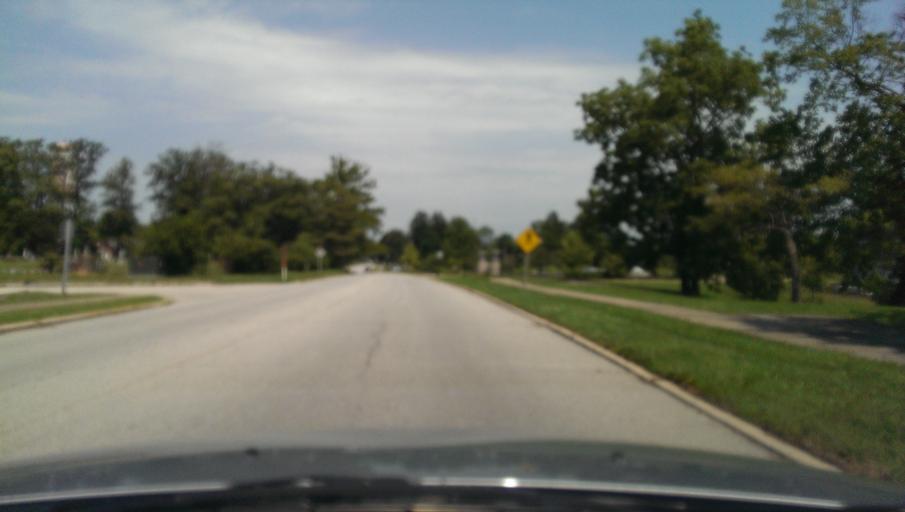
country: US
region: Indiana
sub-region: Marion County
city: Lawrence
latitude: 39.8576
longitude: -86.0103
